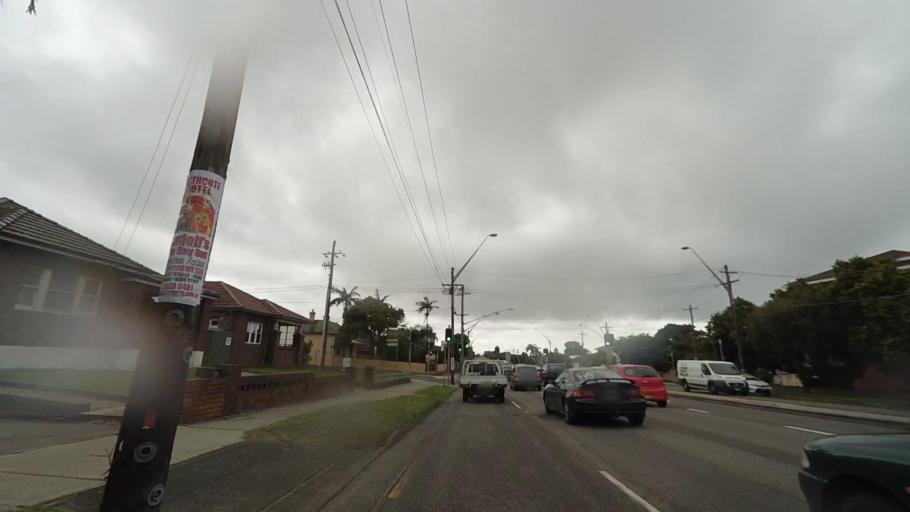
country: AU
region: New South Wales
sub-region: Kogarah
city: Blakehurst
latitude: -34.0015
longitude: 151.1263
